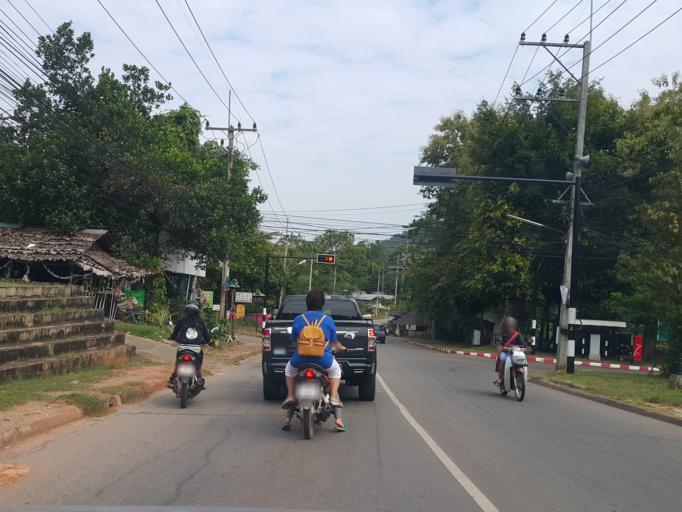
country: TH
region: Mae Hong Son
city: Mae Hong Son
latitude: 19.3045
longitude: 97.9614
